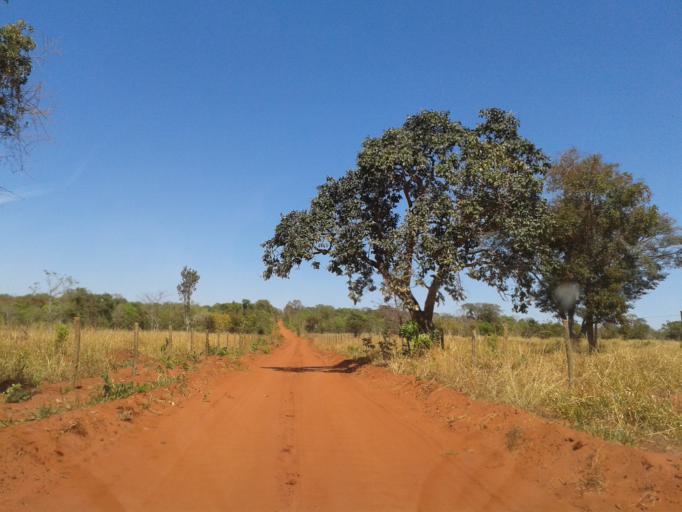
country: BR
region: Minas Gerais
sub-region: Ituiutaba
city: Ituiutaba
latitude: -19.0903
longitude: -49.2655
